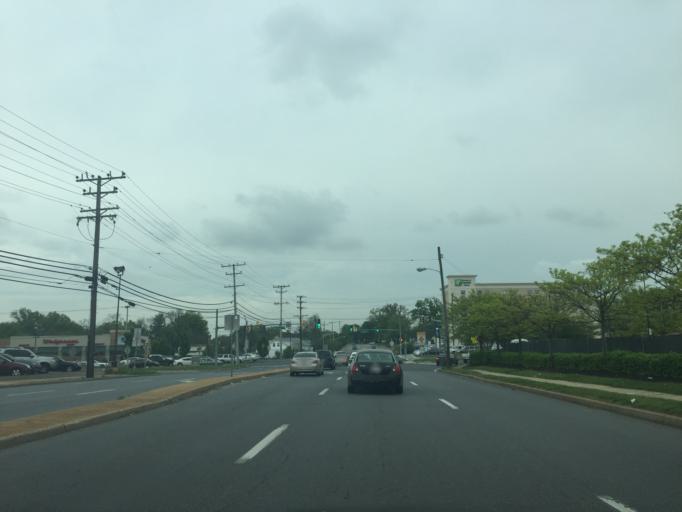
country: US
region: Maryland
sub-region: Baltimore County
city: Catonsville
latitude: 39.2892
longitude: -76.7315
